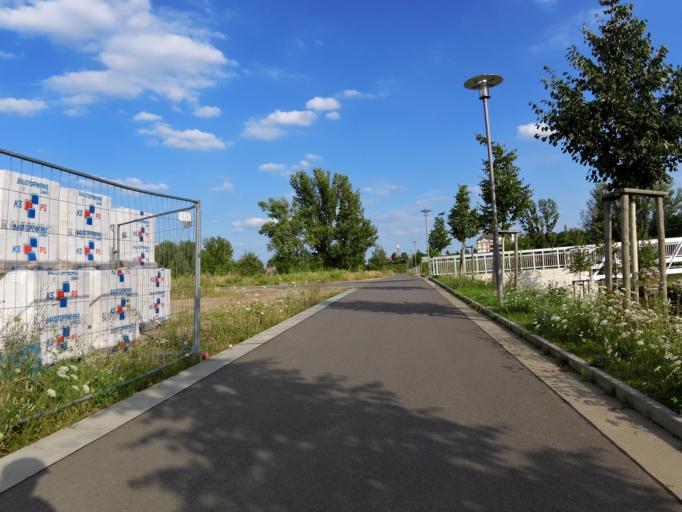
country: DE
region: Saxony
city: Leipzig
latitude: 51.3307
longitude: 12.3049
